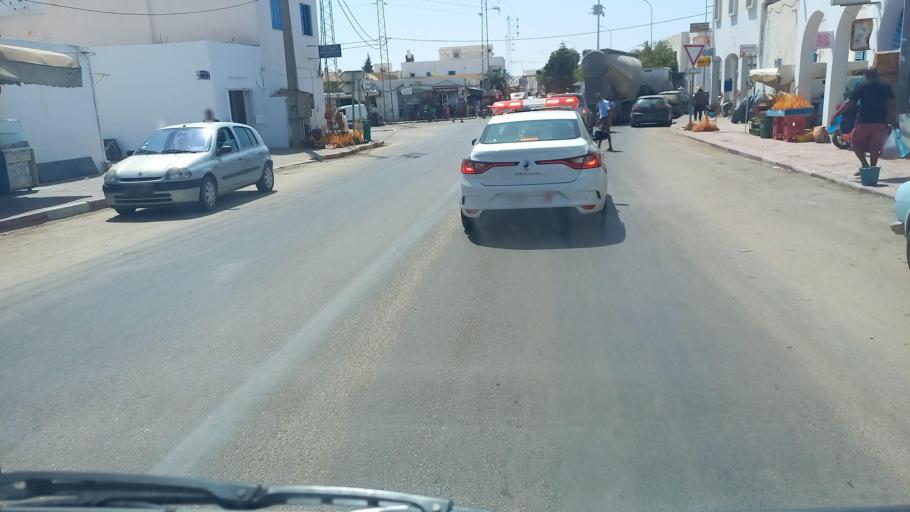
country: TN
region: Madanin
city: Houmt Souk
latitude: 33.8017
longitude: 10.8832
